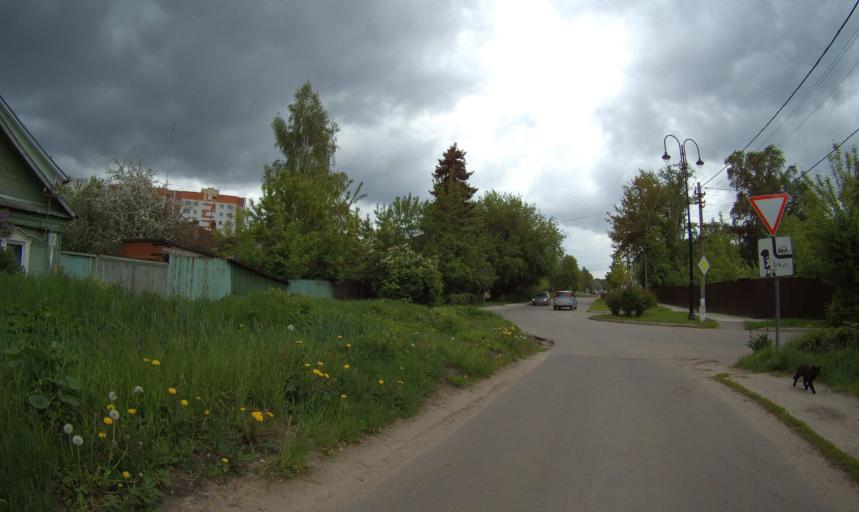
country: RU
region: Moskovskaya
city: Kolomna
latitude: 55.1004
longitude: 38.7780
